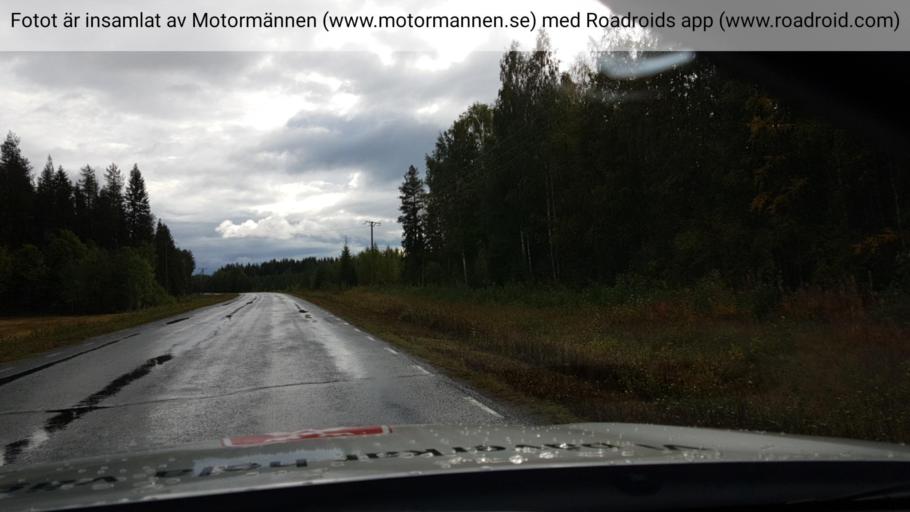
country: SE
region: Norrbotten
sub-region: Bodens Kommun
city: Boden
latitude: 65.8436
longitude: 21.4791
